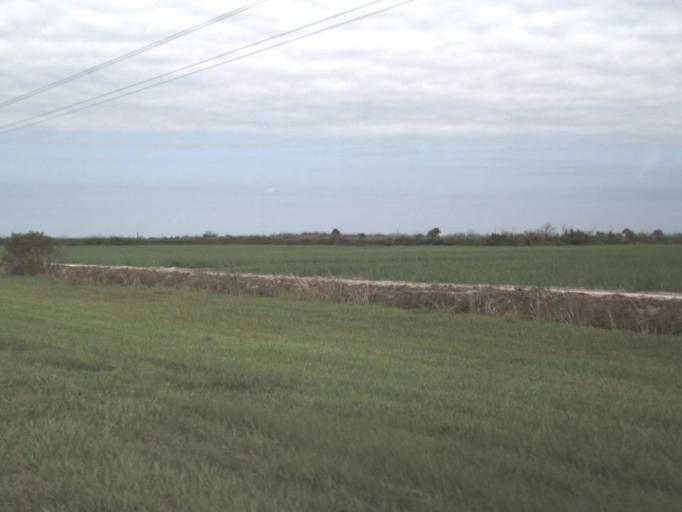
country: US
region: Florida
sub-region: Glades County
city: Moore Haven
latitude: 26.7583
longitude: -81.1559
